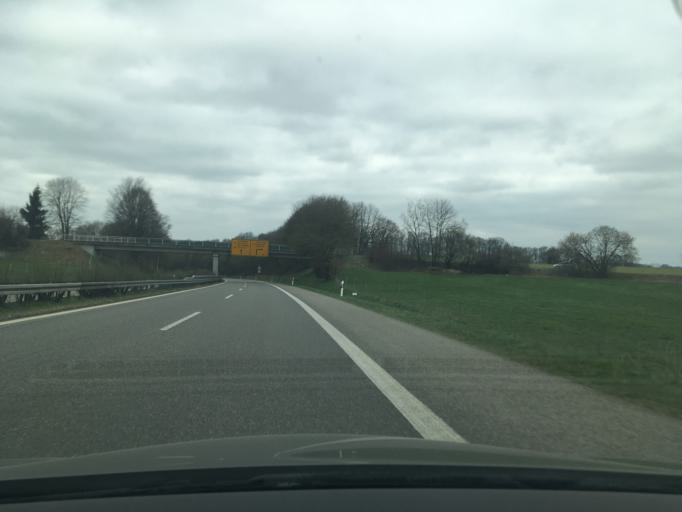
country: DE
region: Baden-Wuerttemberg
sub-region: Tuebingen Region
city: Ummendorf
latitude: 48.0870
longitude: 9.8193
